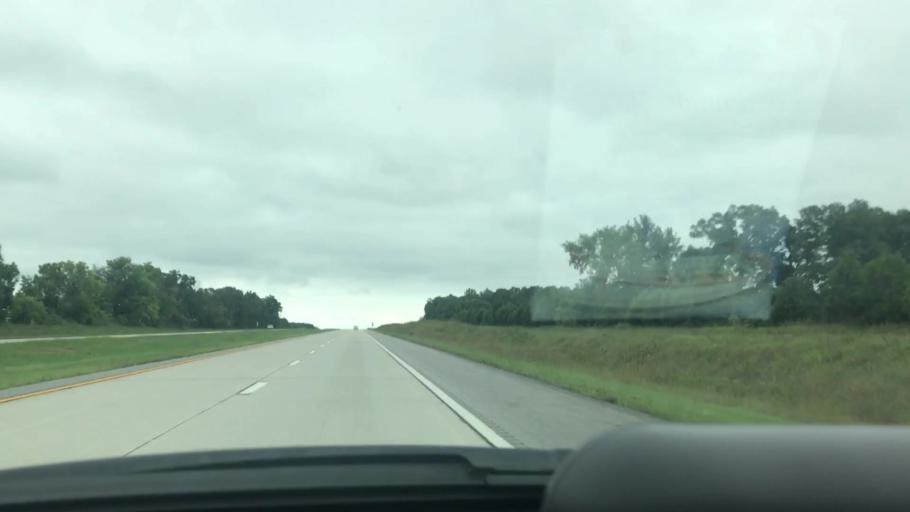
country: US
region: Missouri
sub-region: Greene County
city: Fair Grove
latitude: 37.4802
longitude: -93.1392
